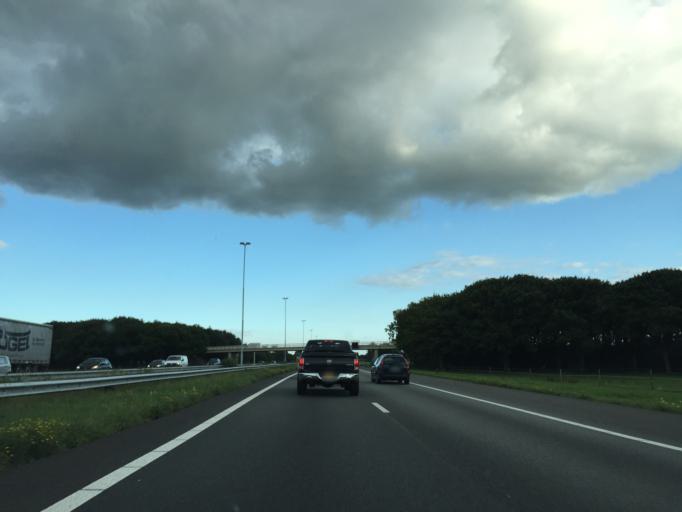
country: NL
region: North Brabant
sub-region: Gemeente Dongen
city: Dongen
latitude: 51.5473
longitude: 4.9745
